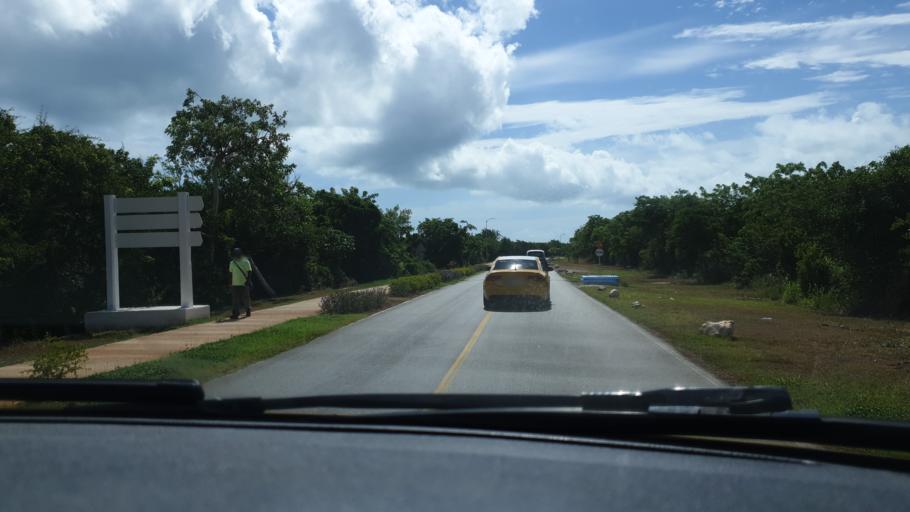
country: CU
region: Sancti Spiritus
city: Yaguajay
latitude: 22.6560
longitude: -79.0372
